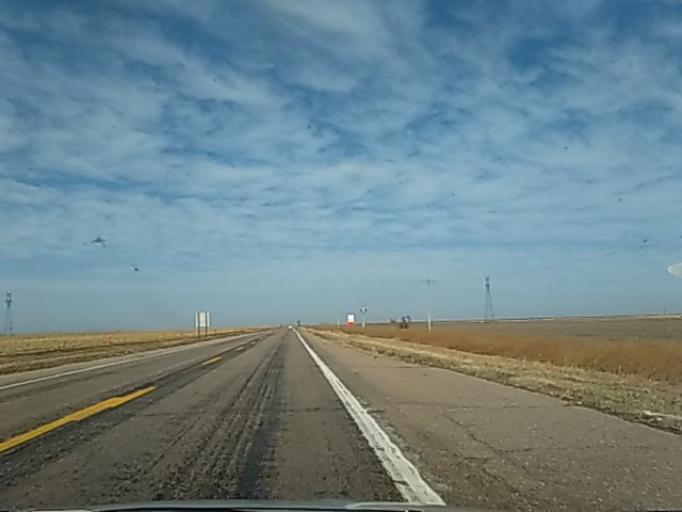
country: US
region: Nebraska
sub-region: Clay County
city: Clay Center
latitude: 40.3744
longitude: -98.0519
